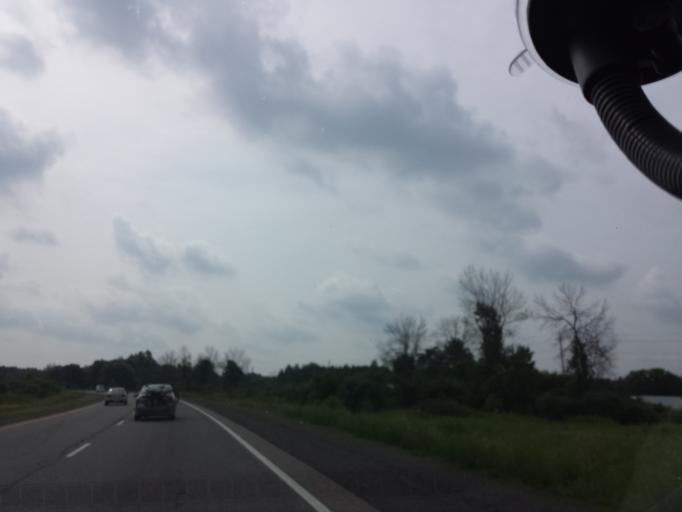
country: CA
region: Ontario
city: Ottawa
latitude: 45.3755
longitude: -75.5731
